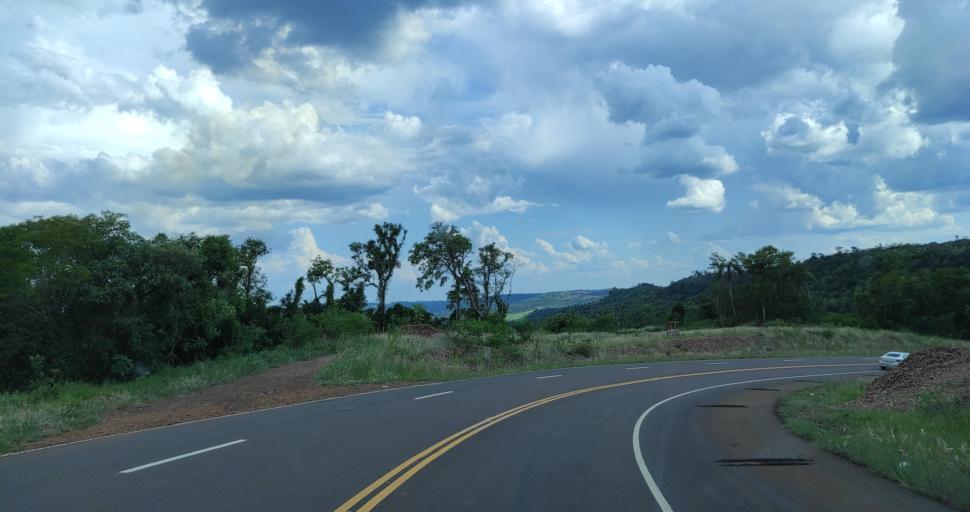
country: AR
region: Misiones
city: Bernardo de Irigoyen
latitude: -26.3031
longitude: -53.8146
